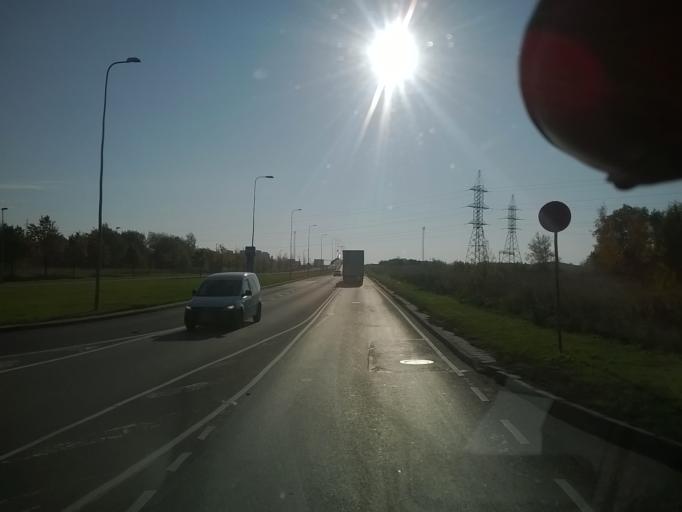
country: EE
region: Harju
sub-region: Tallinna linn
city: Kose
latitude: 59.4254
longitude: 24.8387
